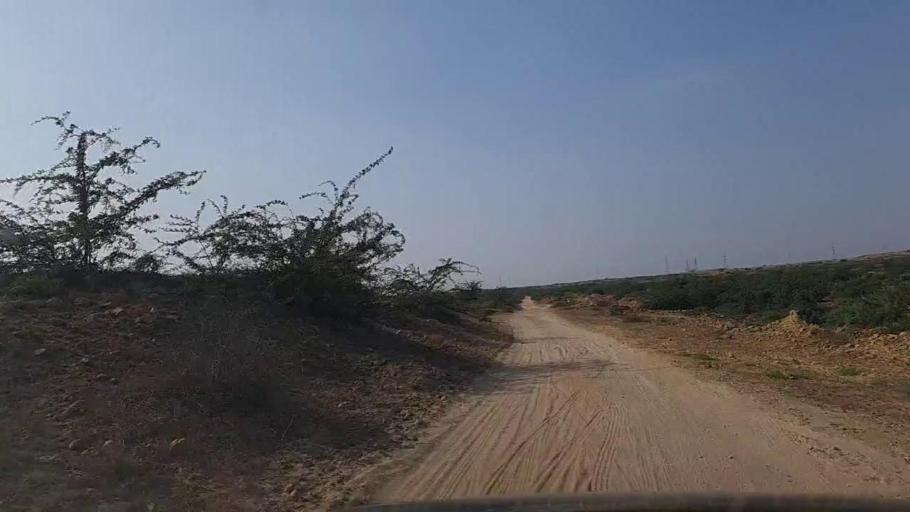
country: PK
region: Sindh
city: Gharo
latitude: 24.7500
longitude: 67.5563
